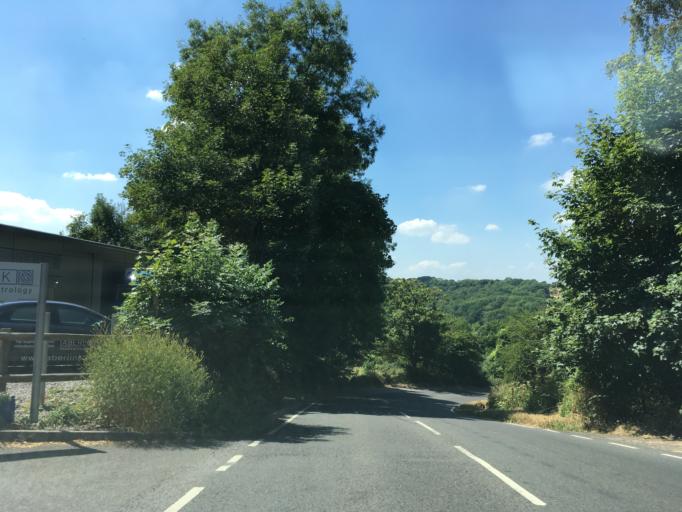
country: GB
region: England
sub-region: Gloucestershire
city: Chalford
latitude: 51.7346
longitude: -2.1677
